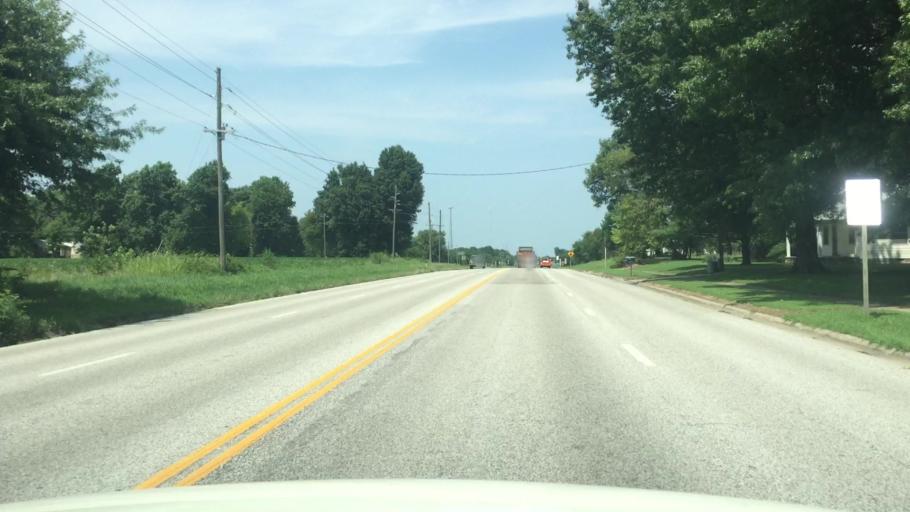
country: US
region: Kansas
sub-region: Cherokee County
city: Galena
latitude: 37.1726
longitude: -94.7044
